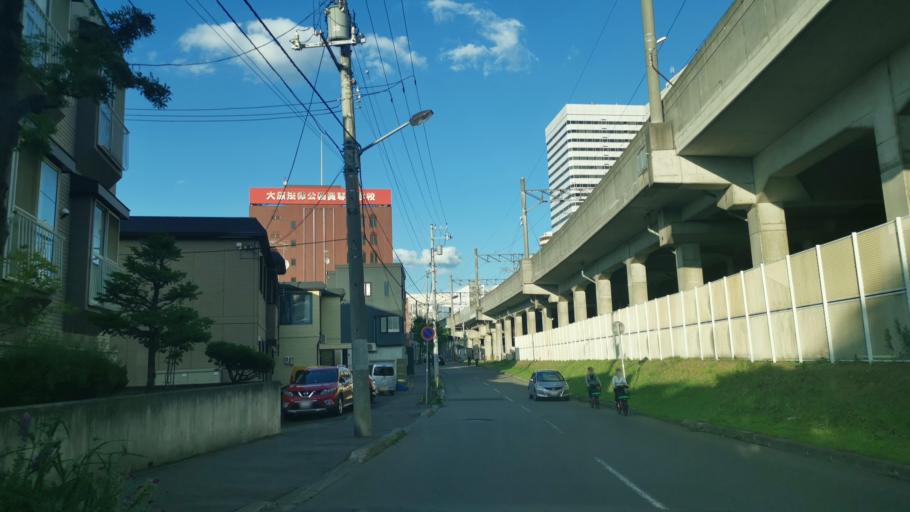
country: JP
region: Hokkaido
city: Sapporo
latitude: 43.0673
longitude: 141.3424
